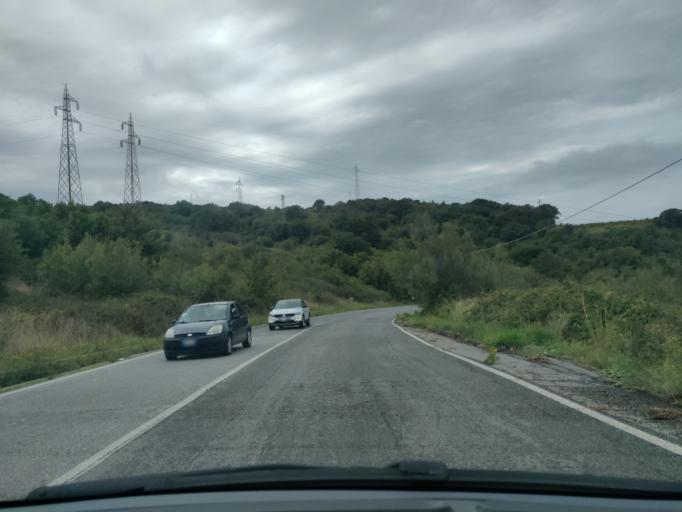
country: IT
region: Latium
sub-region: Citta metropolitana di Roma Capitale
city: Civitavecchia
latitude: 42.1124
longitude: 11.8529
